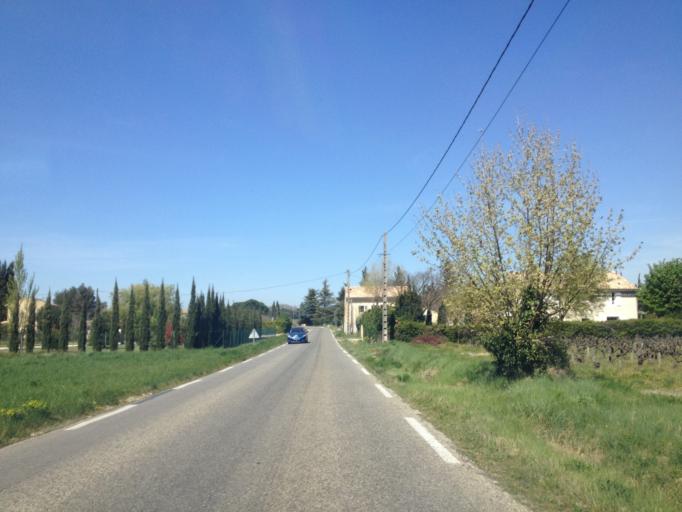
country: FR
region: Provence-Alpes-Cote d'Azur
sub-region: Departement du Vaucluse
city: Orange
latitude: 44.1078
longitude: 4.8204
